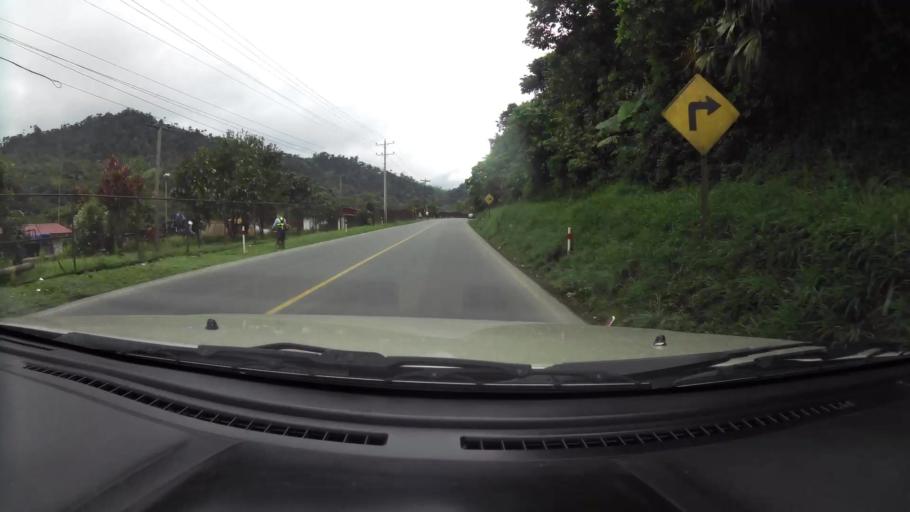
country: EC
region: Santo Domingo de los Tsachilas
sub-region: Canton Santo Domingo de los Colorados
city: Santo Domingo de los Colorados
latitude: -0.2690
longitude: -79.0922
